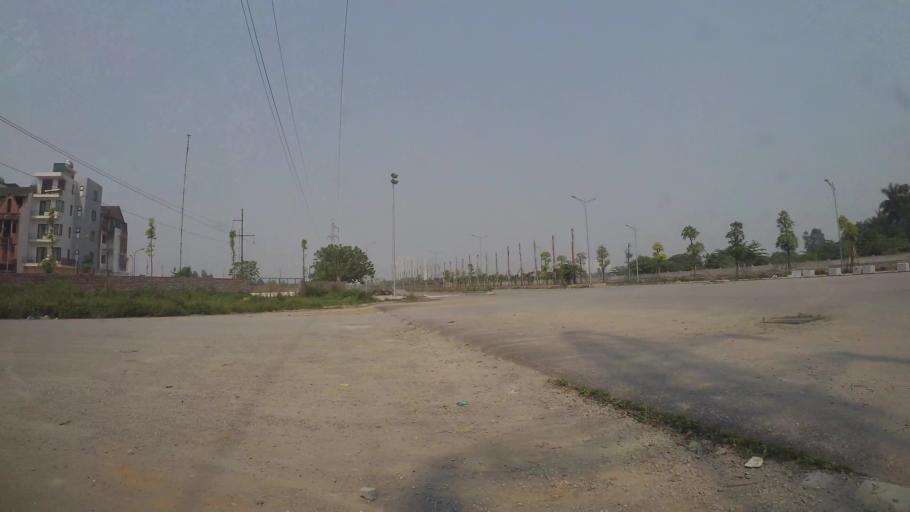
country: VN
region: Ha Noi
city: Ha Dong
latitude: 20.9657
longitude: 105.7995
